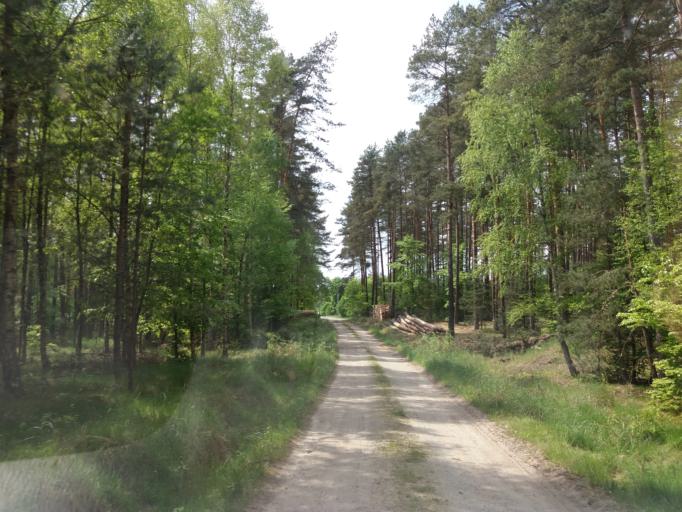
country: PL
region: West Pomeranian Voivodeship
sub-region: Powiat choszczenski
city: Drawno
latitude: 53.1943
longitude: 15.7574
